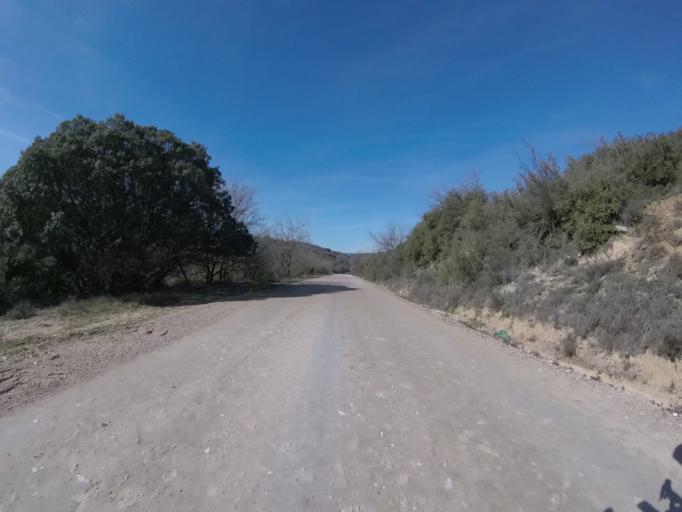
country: ES
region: Navarre
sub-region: Provincia de Navarra
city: Oteiza
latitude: 42.6458
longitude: -1.9631
